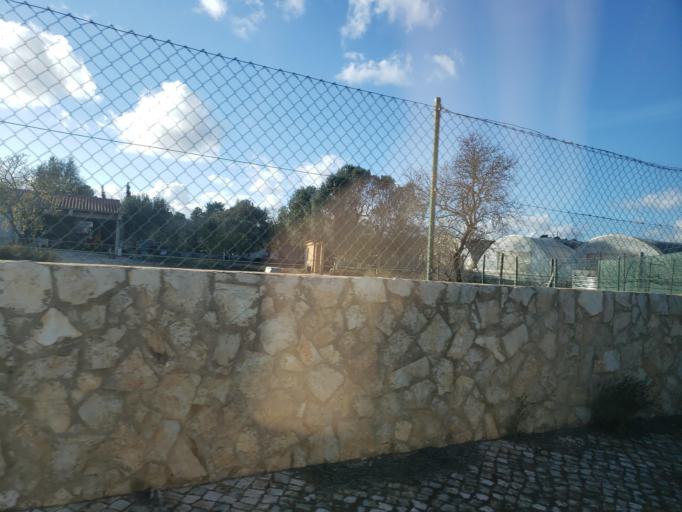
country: PT
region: Faro
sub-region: Portimao
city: Alvor
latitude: 37.1916
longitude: -8.5893
